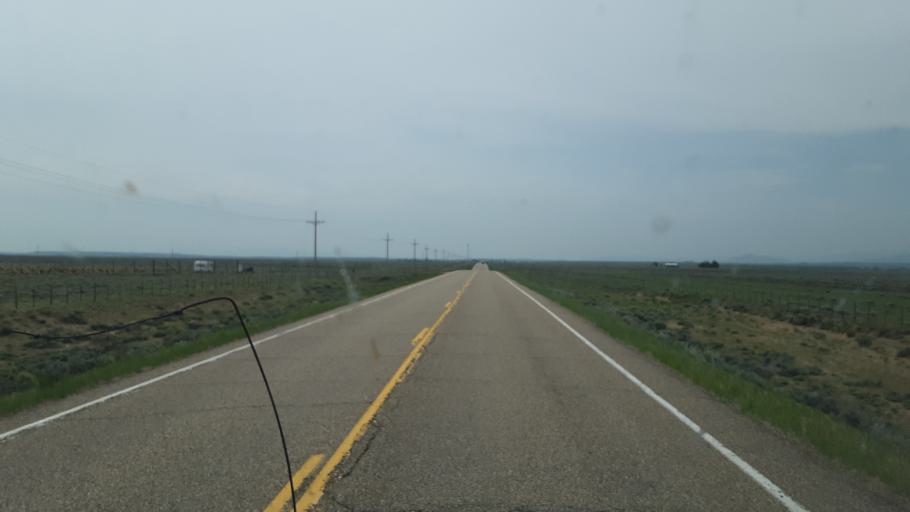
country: US
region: Colorado
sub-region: Jackson County
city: Walden
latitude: 40.8890
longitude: -106.3010
